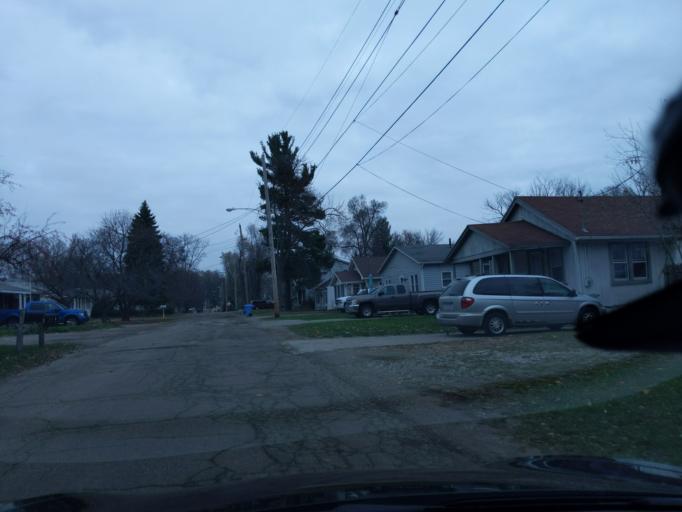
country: US
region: Michigan
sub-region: Ingham County
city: Edgemont Park
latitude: 42.7618
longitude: -84.5707
